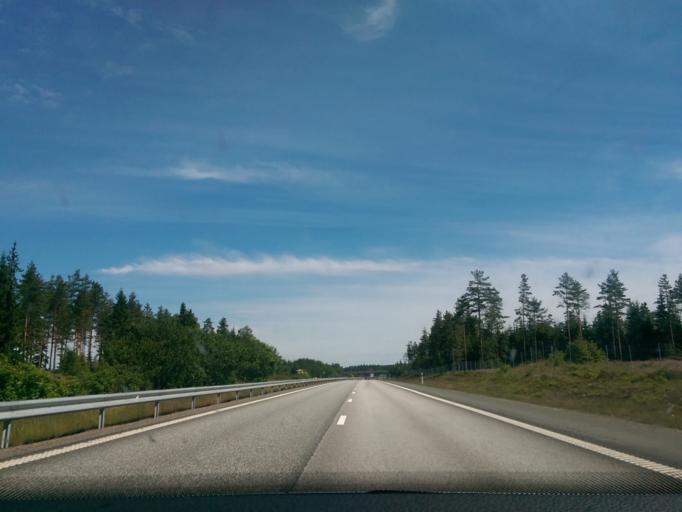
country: SE
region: Joenkoeping
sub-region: Jonkopings Kommun
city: Odensjo
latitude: 57.6162
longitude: 14.1769
